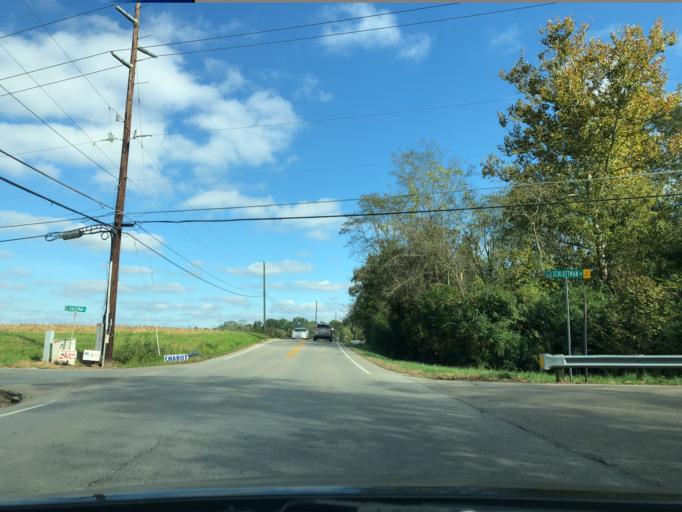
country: US
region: Ohio
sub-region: Hamilton County
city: Loveland
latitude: 39.2811
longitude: -84.2289
